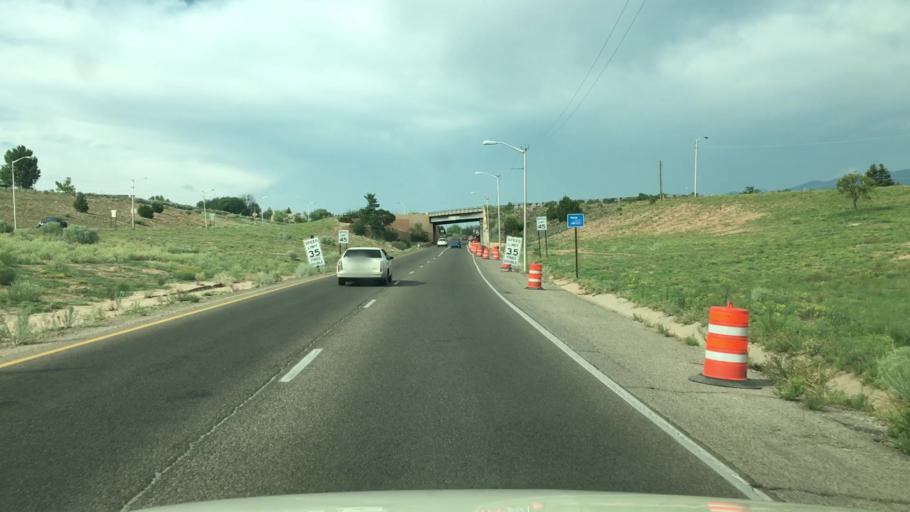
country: US
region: New Mexico
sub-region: Santa Fe County
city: Santa Fe
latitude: 35.6971
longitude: -105.9532
